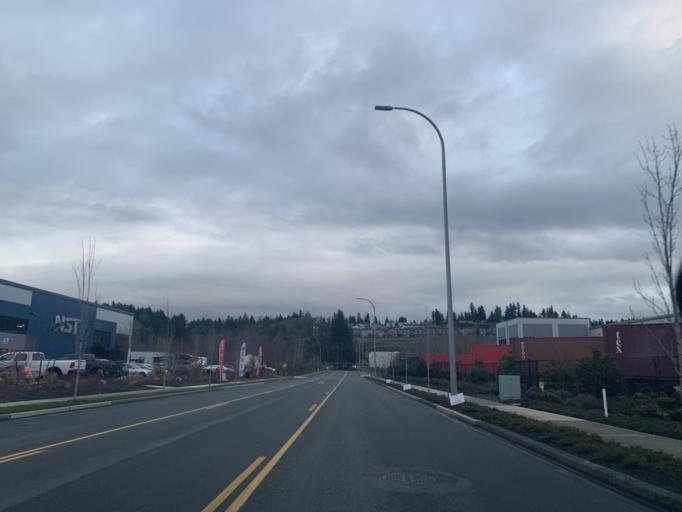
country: US
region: Washington
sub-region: Pierce County
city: Milton
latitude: 47.2335
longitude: -122.3299
